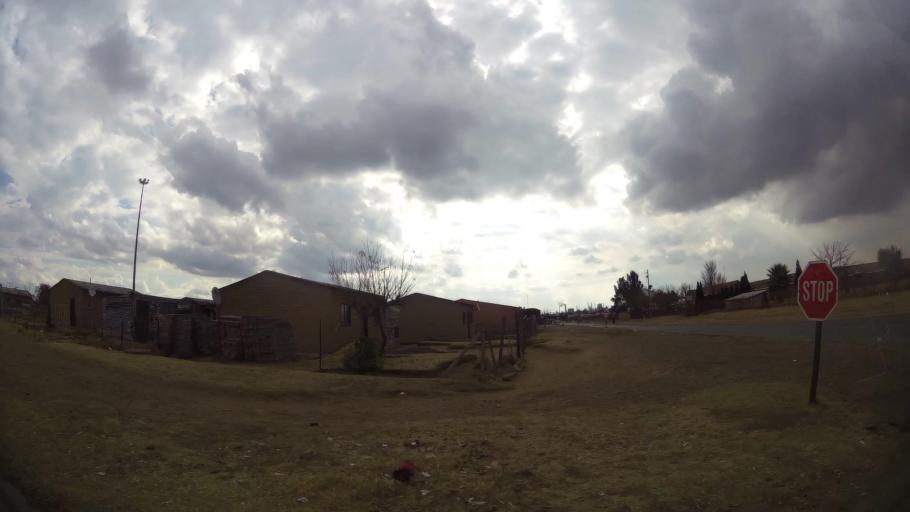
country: ZA
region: Orange Free State
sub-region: Fezile Dabi District Municipality
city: Sasolburg
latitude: -26.8541
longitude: 27.8548
